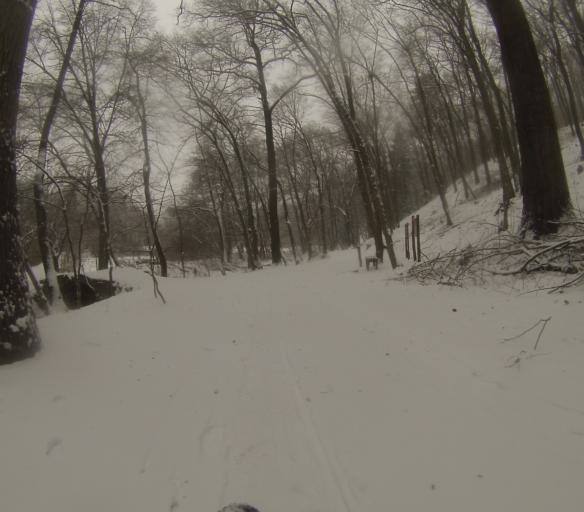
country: CZ
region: South Moravian
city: Strelice
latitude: 49.1308
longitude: 16.5082
